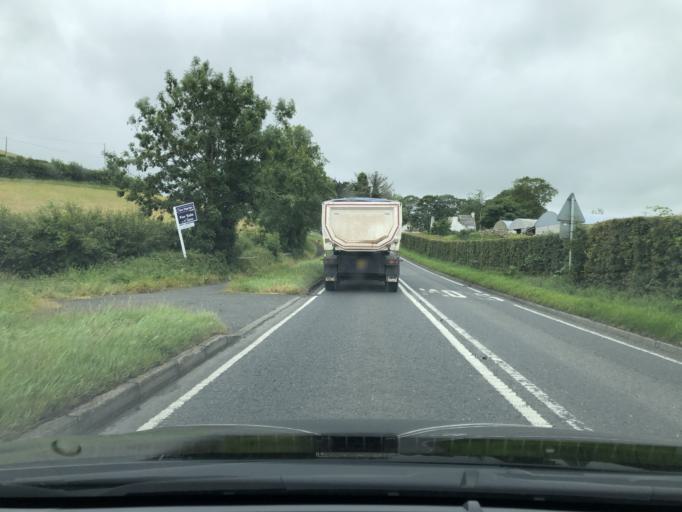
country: GB
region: Northern Ireland
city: Ballynahinch
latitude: 54.3681
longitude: -5.8595
